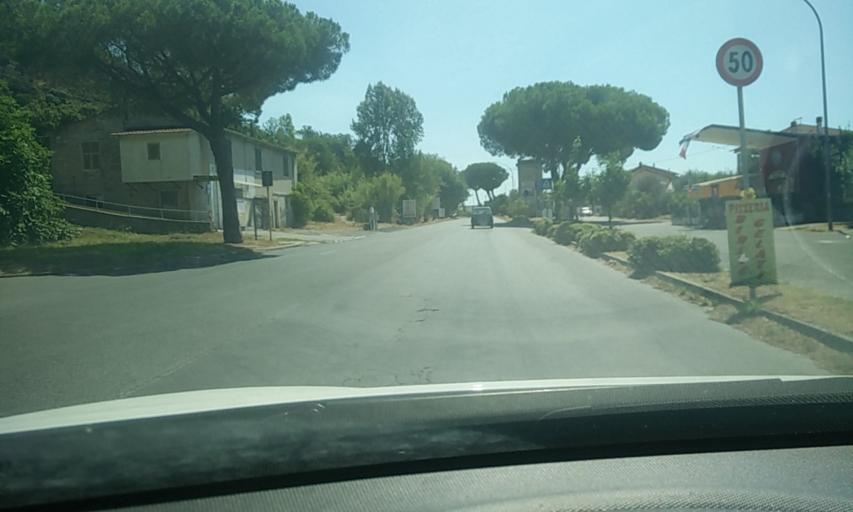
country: IT
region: Tuscany
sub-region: Provincia di Massa-Carrara
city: Massa
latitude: 44.0388
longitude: 10.0957
